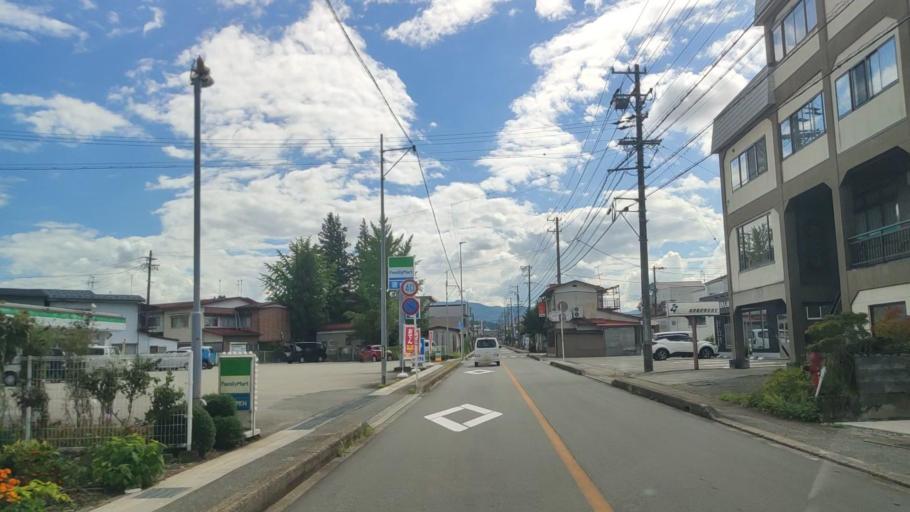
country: JP
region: Gifu
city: Takayama
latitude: 36.1600
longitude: 137.2524
